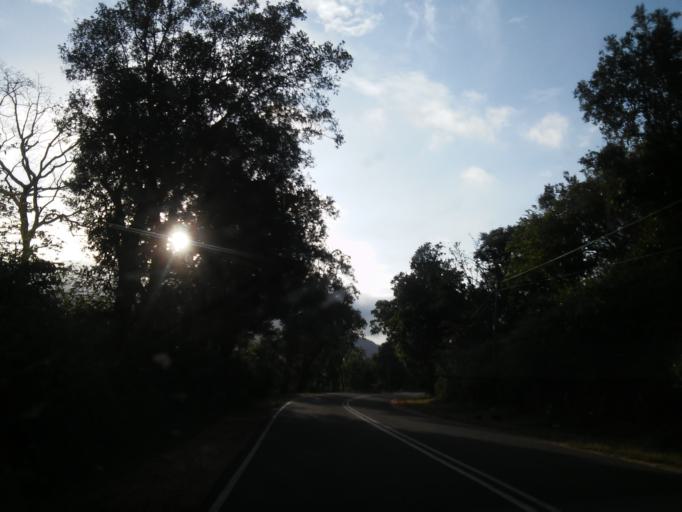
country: LK
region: Central
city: Sigiriya
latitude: 8.0952
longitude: 80.6171
